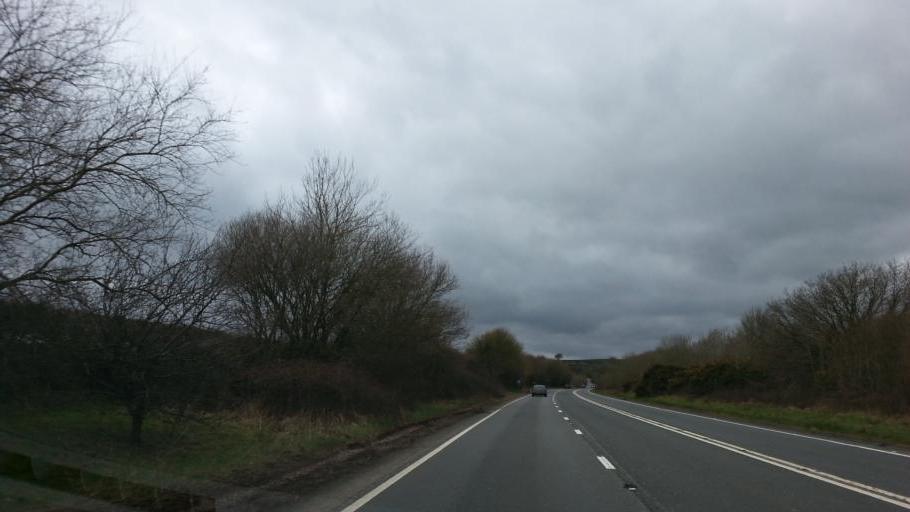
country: GB
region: England
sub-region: Devon
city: Tiverton
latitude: 50.9290
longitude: -3.5375
